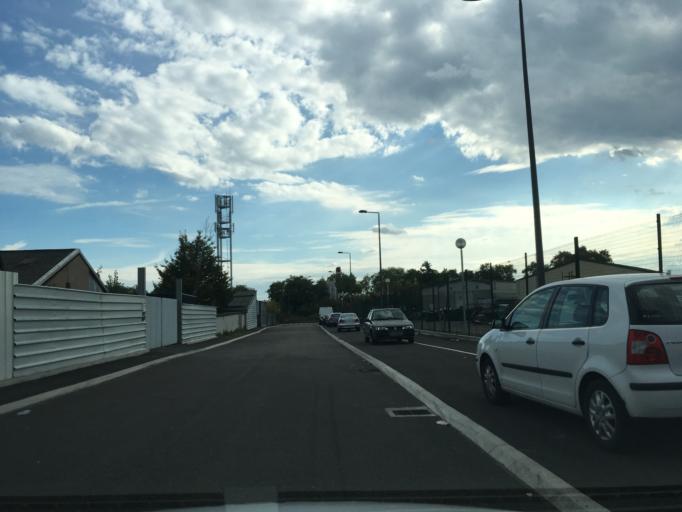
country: FR
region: Alsace
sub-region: Departement du Haut-Rhin
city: Colmar
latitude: 48.0905
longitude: 7.3538
